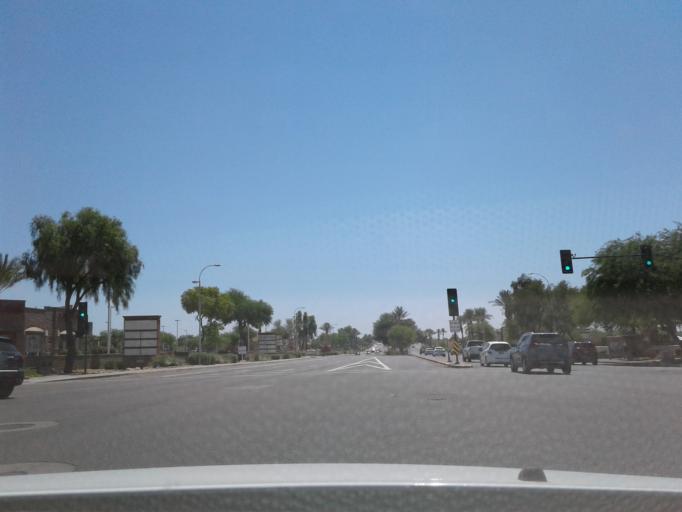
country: US
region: Arizona
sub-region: Maricopa County
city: Guadalupe
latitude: 33.3198
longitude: -111.9806
